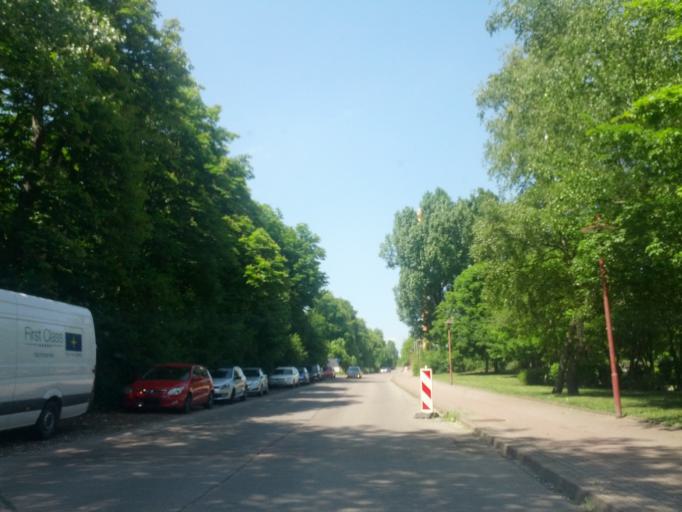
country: DE
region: Thuringia
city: Gotha
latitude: 50.9382
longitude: 10.6771
